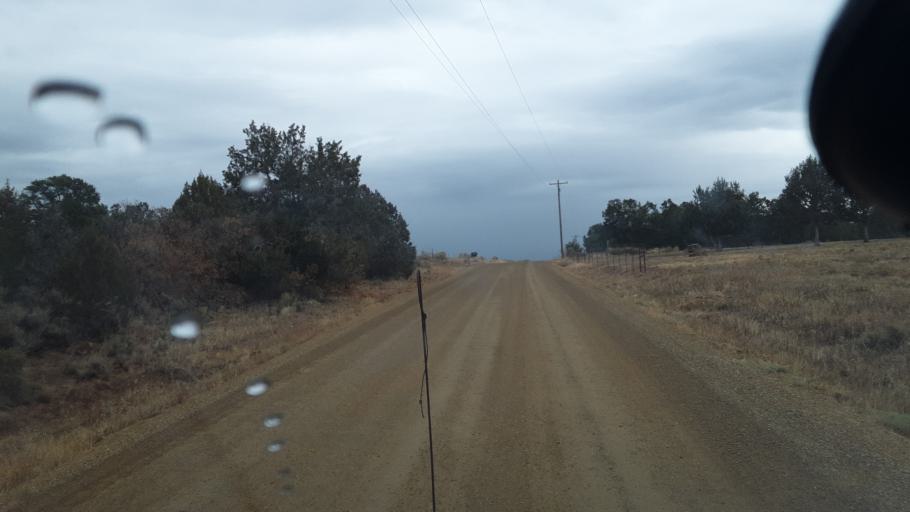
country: US
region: Colorado
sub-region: Montezuma County
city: Mancos
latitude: 37.1984
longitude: -108.1339
